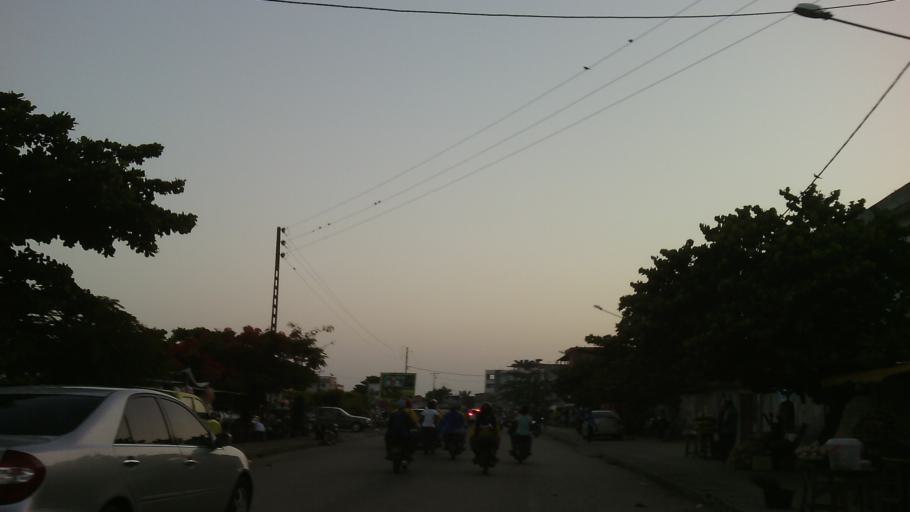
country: BJ
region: Littoral
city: Cotonou
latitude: 6.3674
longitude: 2.3920
